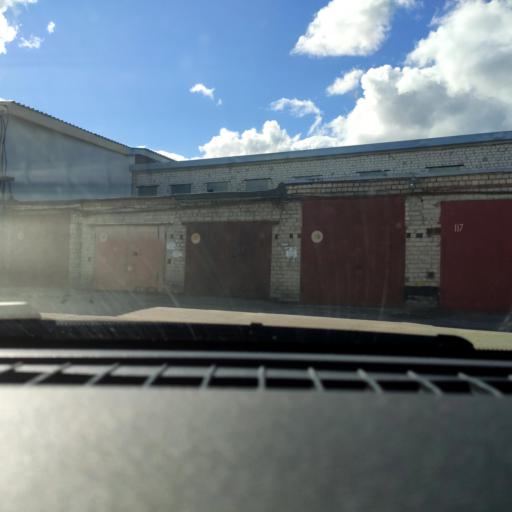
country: RU
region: Voronezj
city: Voronezh
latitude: 51.6655
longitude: 39.2907
